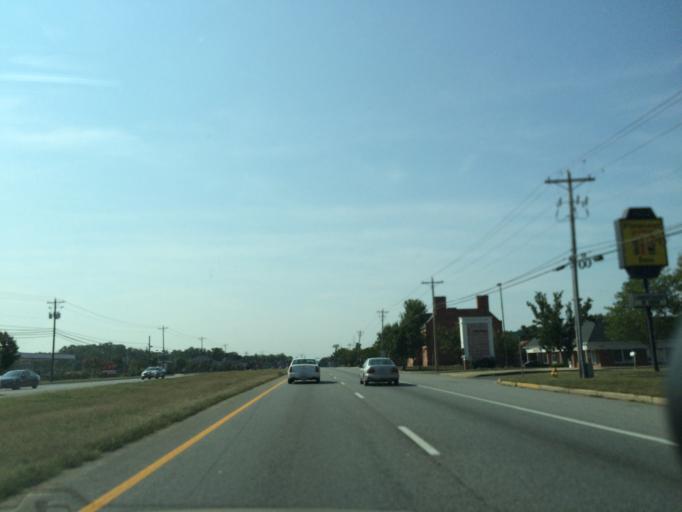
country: US
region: Maryland
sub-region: Charles County
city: La Plata
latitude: 38.5431
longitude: -76.9848
